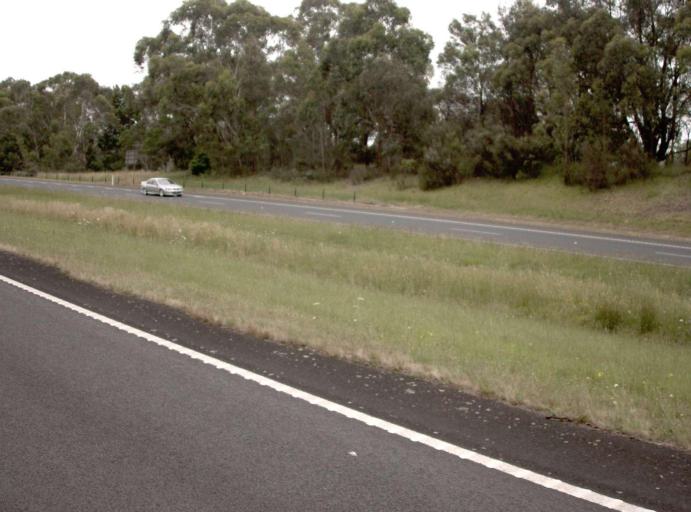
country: AU
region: Victoria
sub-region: Baw Baw
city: Warragul
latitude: -38.0959
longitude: 145.8423
